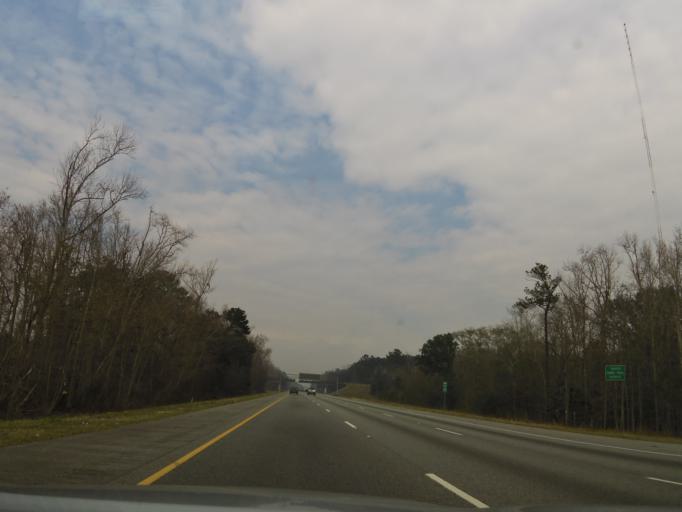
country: US
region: Georgia
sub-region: Liberty County
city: Midway
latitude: 31.6930
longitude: -81.3912
